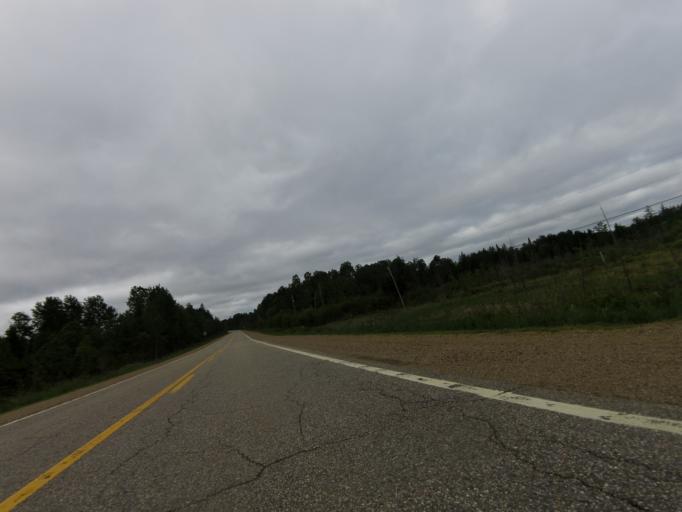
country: CA
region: Quebec
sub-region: Outaouais
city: Shawville
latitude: 45.8766
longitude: -76.4006
